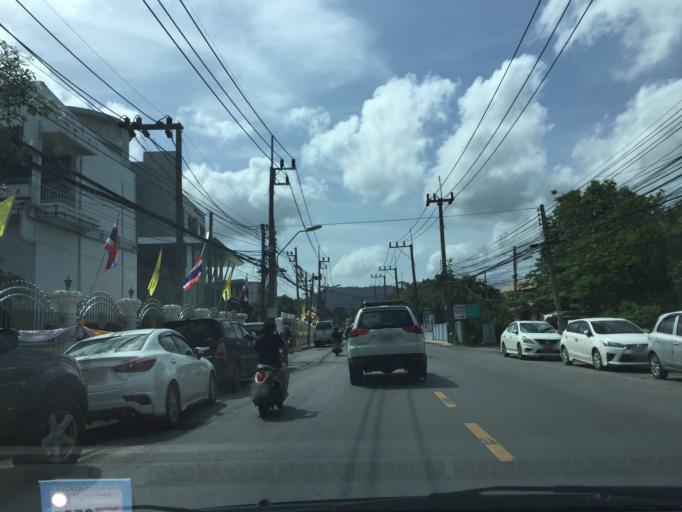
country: TH
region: Phuket
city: Wichit
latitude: 7.8975
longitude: 98.3839
